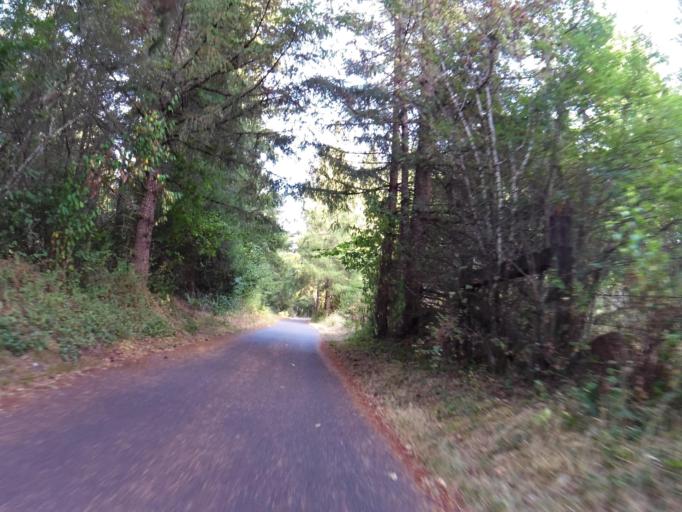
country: US
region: Washington
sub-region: Thurston County
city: Rainier
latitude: 46.8748
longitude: -122.7232
